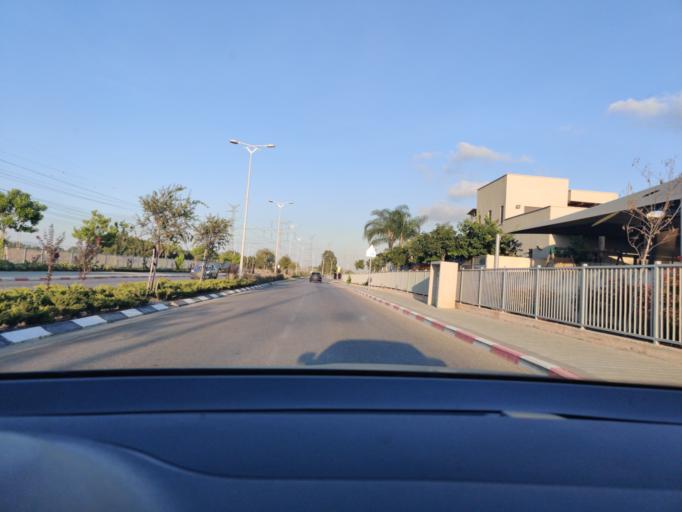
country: IL
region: Central District
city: Elyakhin
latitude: 32.4374
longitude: 34.9416
